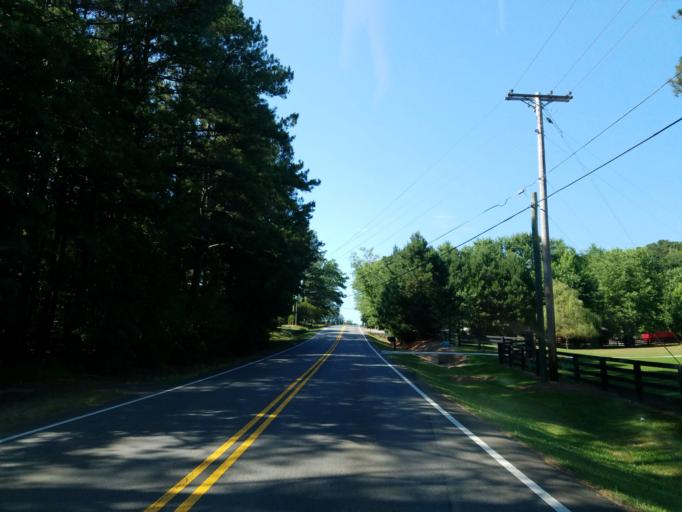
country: US
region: Georgia
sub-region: Fulton County
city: Milton
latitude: 34.2107
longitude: -84.2895
